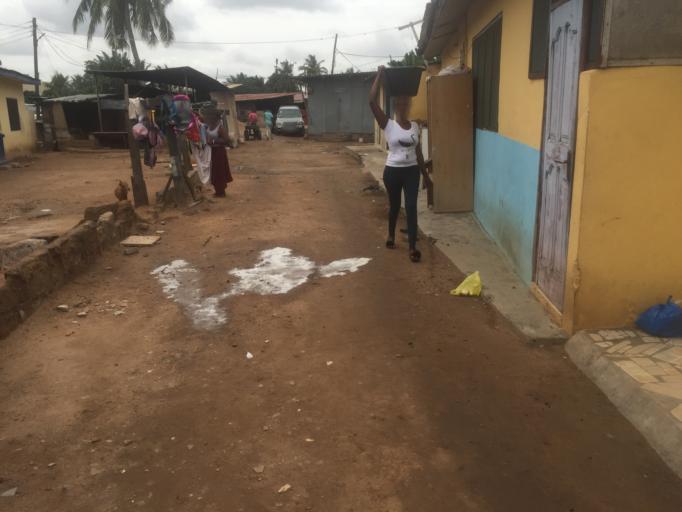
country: GH
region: Greater Accra
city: Dome
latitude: 5.6016
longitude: -0.2244
